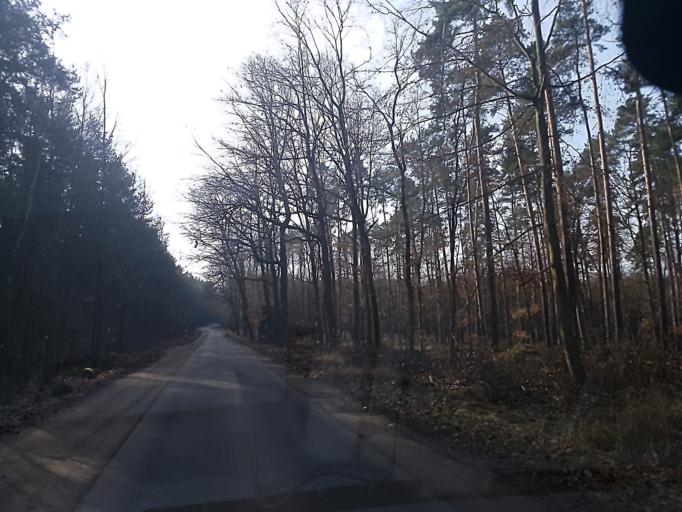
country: DE
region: Brandenburg
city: Wenzlow
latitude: 52.3491
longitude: 12.4624
